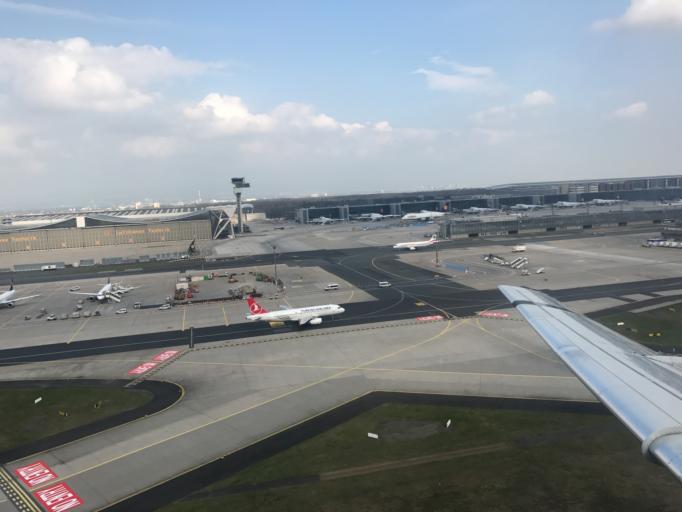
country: DE
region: Hesse
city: Kelsterbach
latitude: 50.0391
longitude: 8.5615
